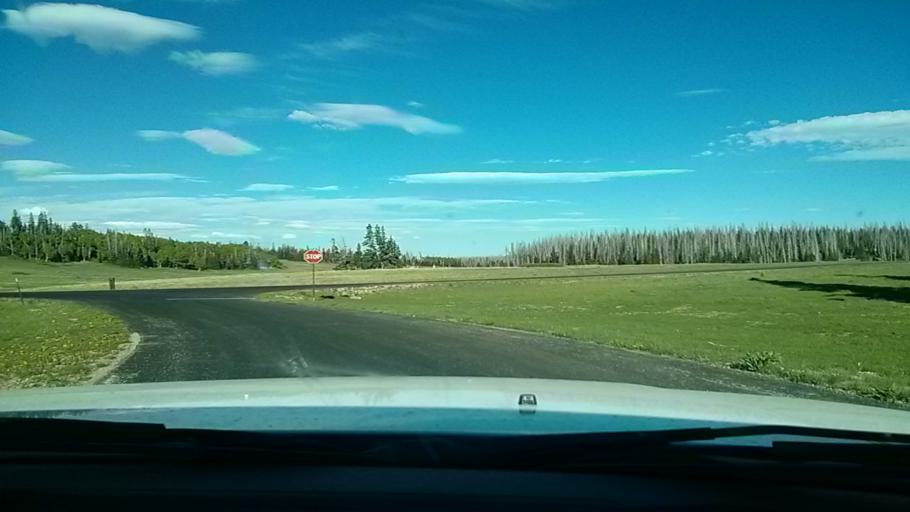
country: US
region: Utah
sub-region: Iron County
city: Parowan
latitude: 37.6308
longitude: -112.8315
